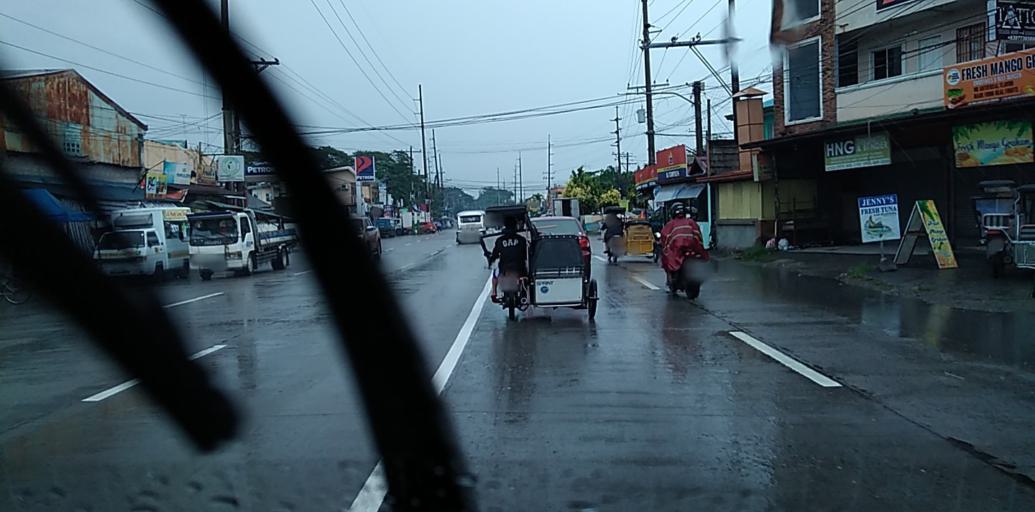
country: PH
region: Central Luzon
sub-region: Province of Pampanga
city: Mexico
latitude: 15.0535
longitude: 120.7105
